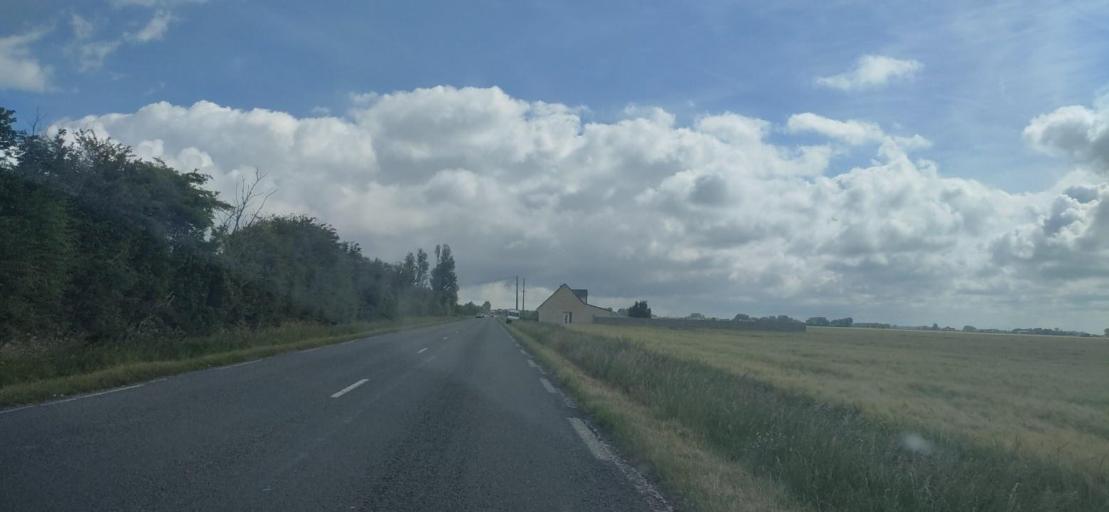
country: FR
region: Nord-Pas-de-Calais
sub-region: Departement du Pas-de-Calais
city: Oye-Plage
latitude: 50.9685
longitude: 2.0167
